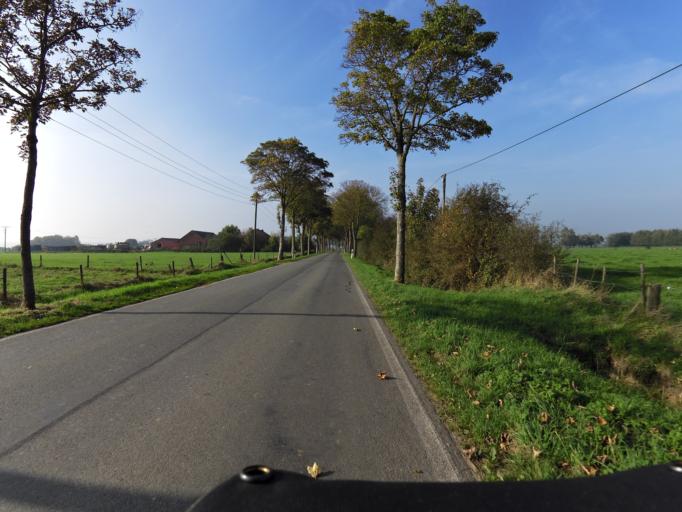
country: DE
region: North Rhine-Westphalia
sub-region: Regierungsbezirk Dusseldorf
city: Kranenburg
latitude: 51.8258
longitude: 6.0059
